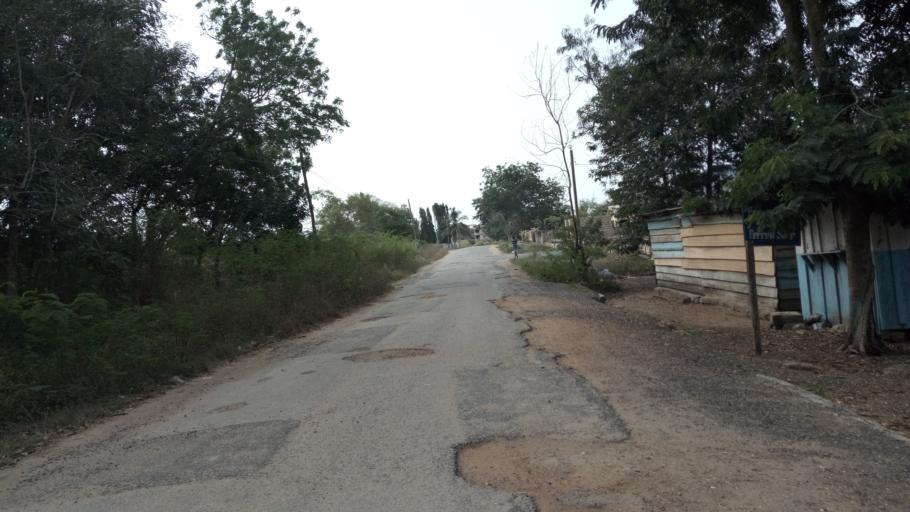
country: GH
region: Central
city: Winneba
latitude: 5.3702
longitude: -0.6414
